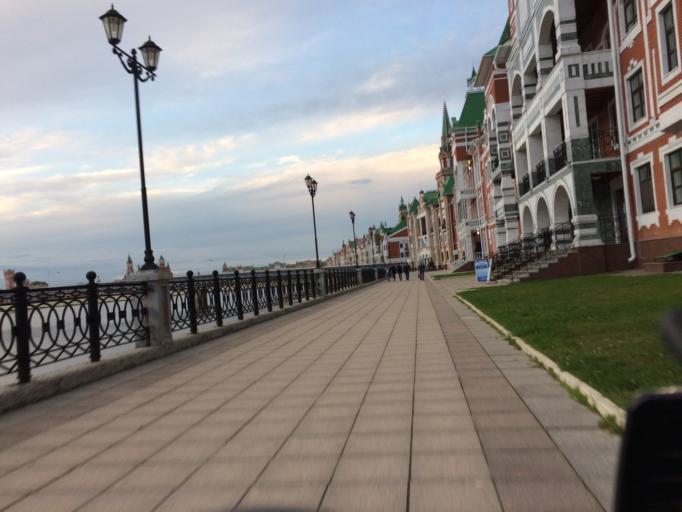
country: RU
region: Mariy-El
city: Yoshkar-Ola
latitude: 56.6311
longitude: 47.9071
